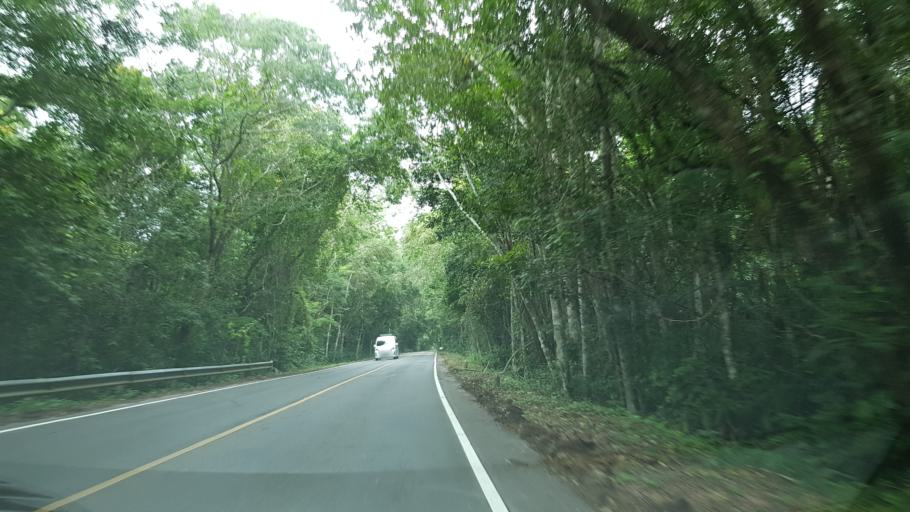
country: GT
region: Peten
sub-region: Municipio de San Jose
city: San Jose
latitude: 17.1753
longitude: -89.6410
